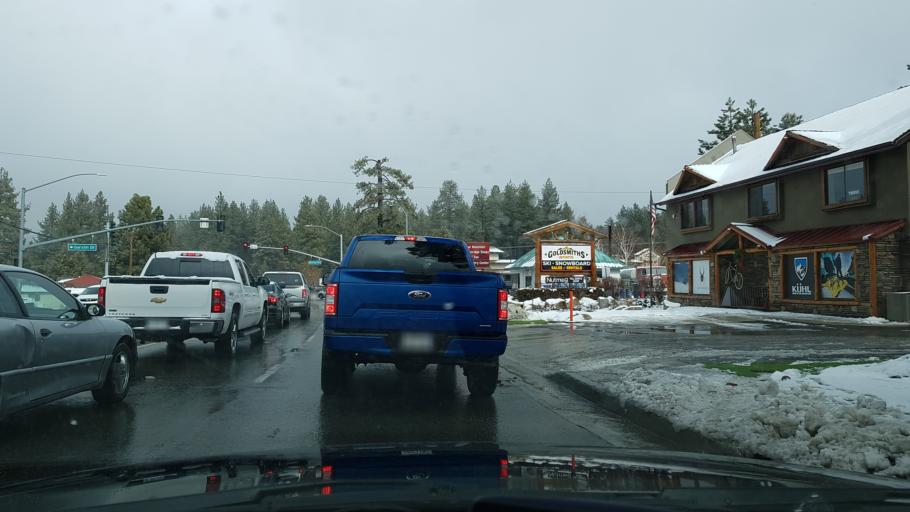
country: US
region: California
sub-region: San Bernardino County
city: Big Bear Lake
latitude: 34.2441
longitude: -116.8845
